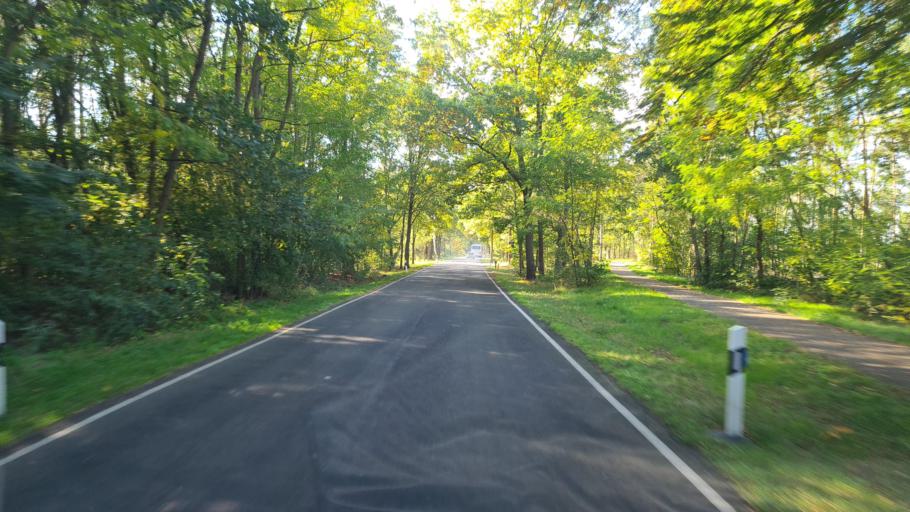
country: DE
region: Brandenburg
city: Kolkwitz
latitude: 51.7634
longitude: 14.2791
